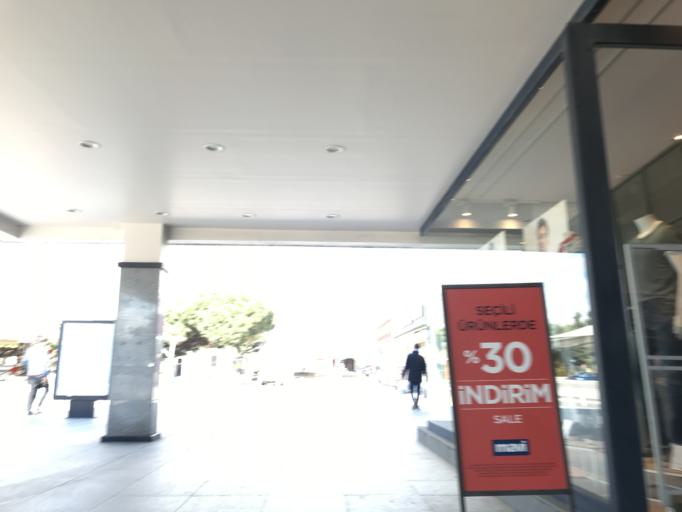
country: TR
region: Istanbul
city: Maltepe
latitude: 40.9260
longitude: 29.1248
